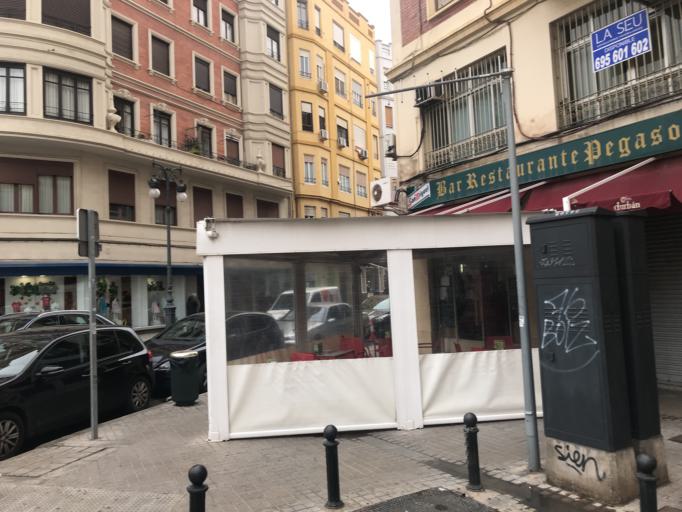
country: ES
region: Valencia
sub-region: Provincia de Valencia
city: Valencia
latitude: 39.4704
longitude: -0.3837
